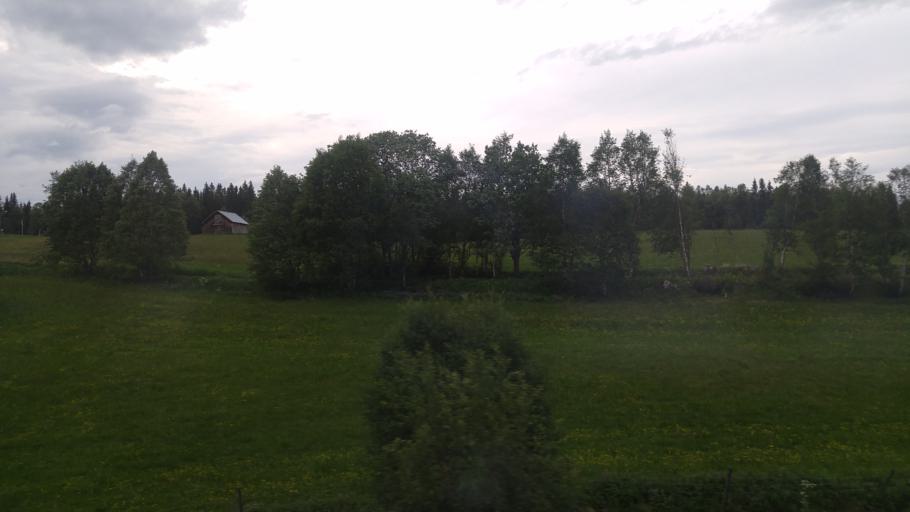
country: SE
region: Jaemtland
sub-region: Are Kommun
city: Are
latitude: 63.3594
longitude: 12.6150
